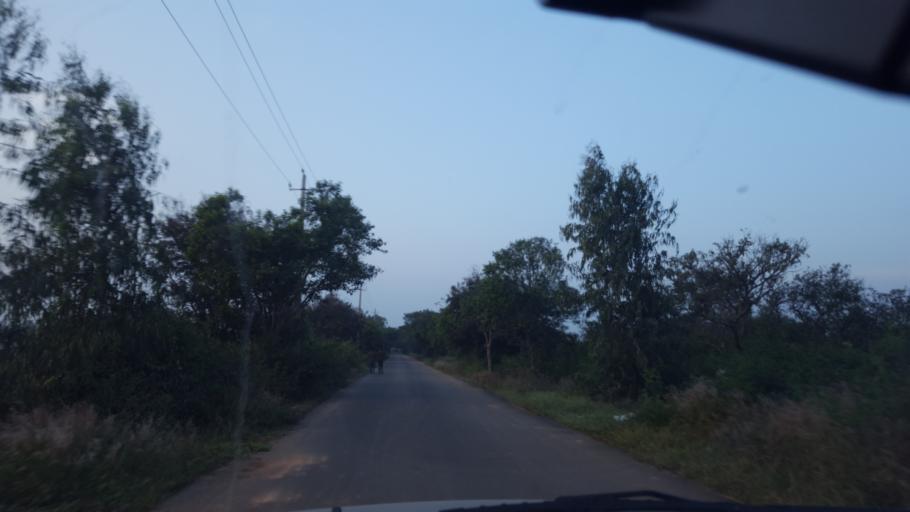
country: IN
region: Karnataka
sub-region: Bangalore Rural
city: Hoskote
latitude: 13.0805
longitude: 77.7032
